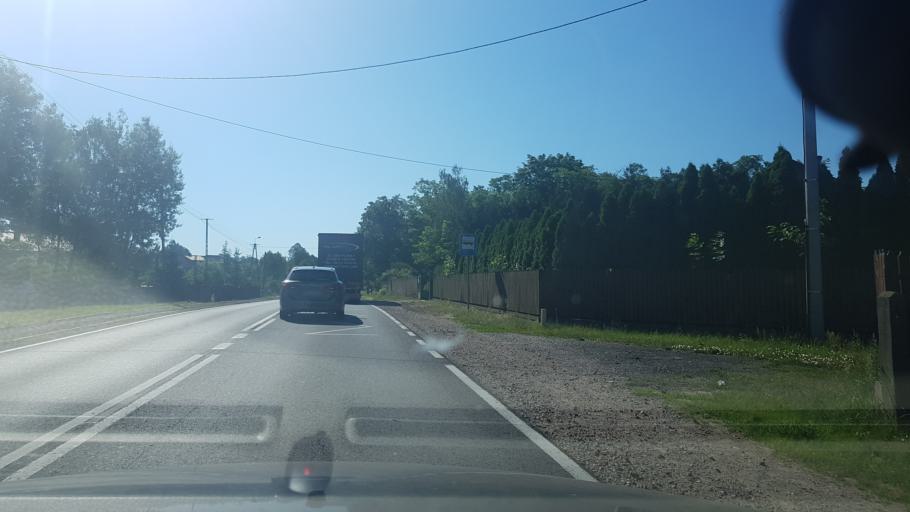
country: PL
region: Masovian Voivodeship
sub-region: Powiat wegrowski
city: Lochow
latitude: 52.5431
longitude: 21.6441
